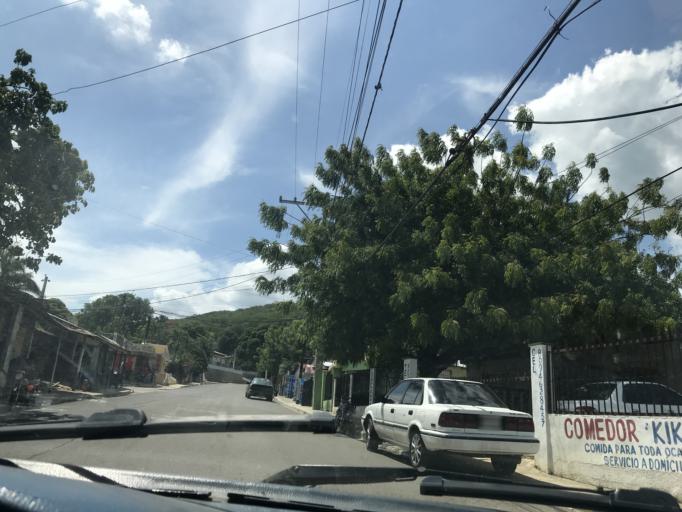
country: DO
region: Santiago
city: Tamboril
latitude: 19.5031
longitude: -70.6515
